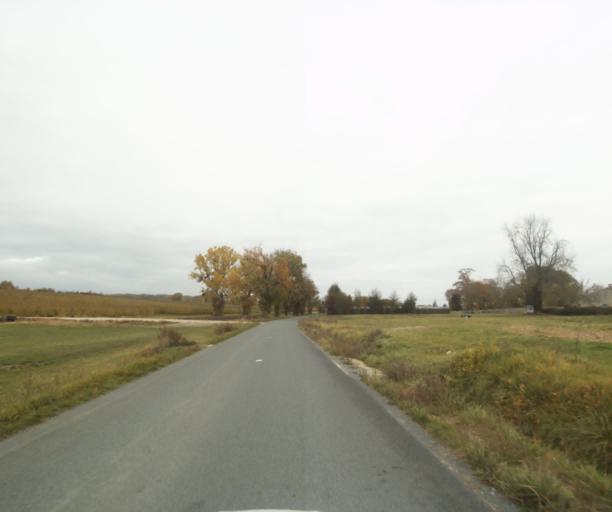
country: FR
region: Poitou-Charentes
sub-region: Departement de la Charente-Maritime
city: Chermignac
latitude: 45.7104
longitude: -0.6884
